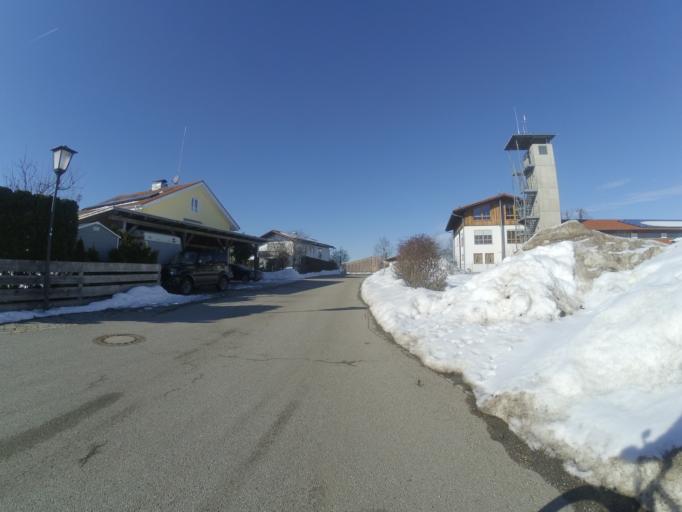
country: DE
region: Bavaria
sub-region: Upper Bavaria
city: Aying
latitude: 47.9447
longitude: 11.7966
